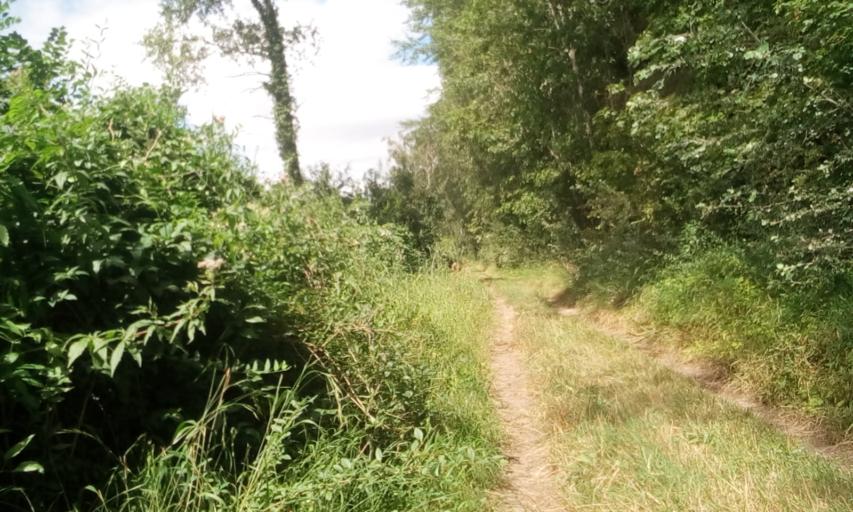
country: FR
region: Lower Normandy
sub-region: Departement du Calvados
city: Bellengreville
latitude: 49.1539
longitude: -0.2058
